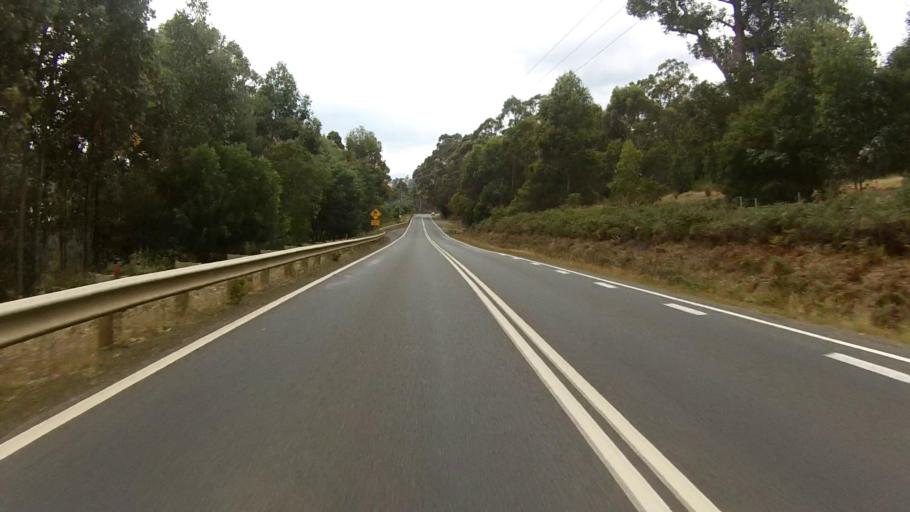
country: AU
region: Tasmania
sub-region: Huon Valley
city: Huonville
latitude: -43.0604
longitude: 147.0423
